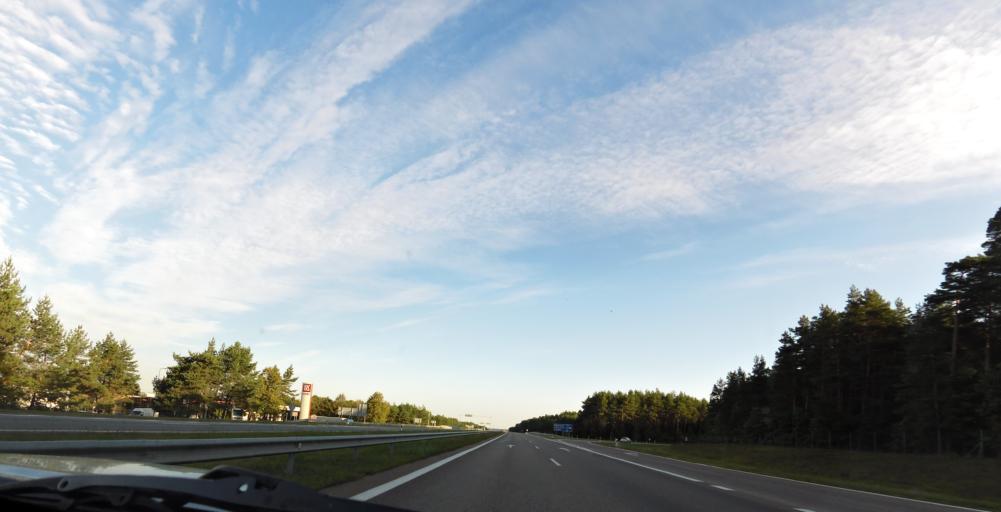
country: LT
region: Vilnius County
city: Ukmerge
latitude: 55.2682
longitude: 24.8118
